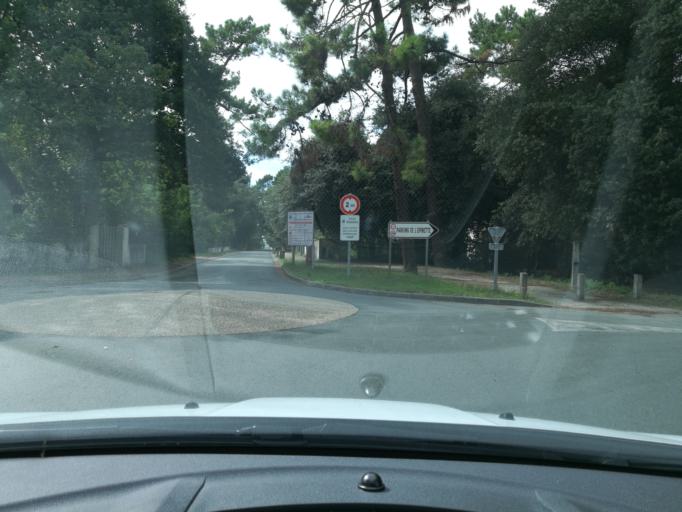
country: FR
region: Poitou-Charentes
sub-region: Departement de la Charente-Maritime
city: Saint-Trojan-les-Bains
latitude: 45.8595
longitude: -1.2410
